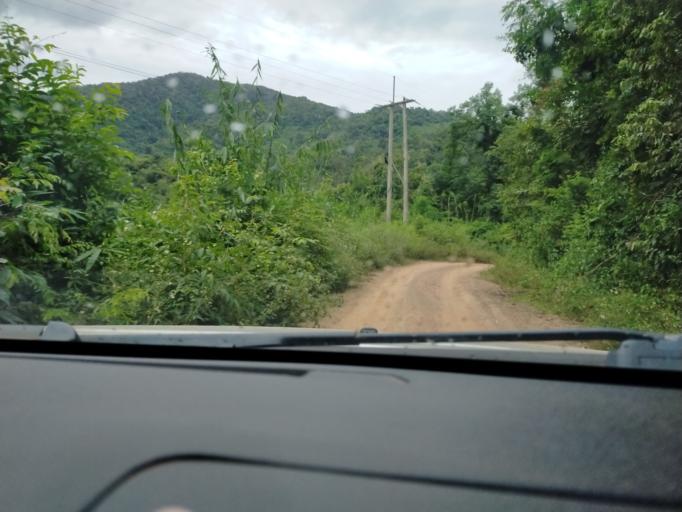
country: TH
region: Nan
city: Chaloem Phra Kiat
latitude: 19.8113
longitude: 101.3608
